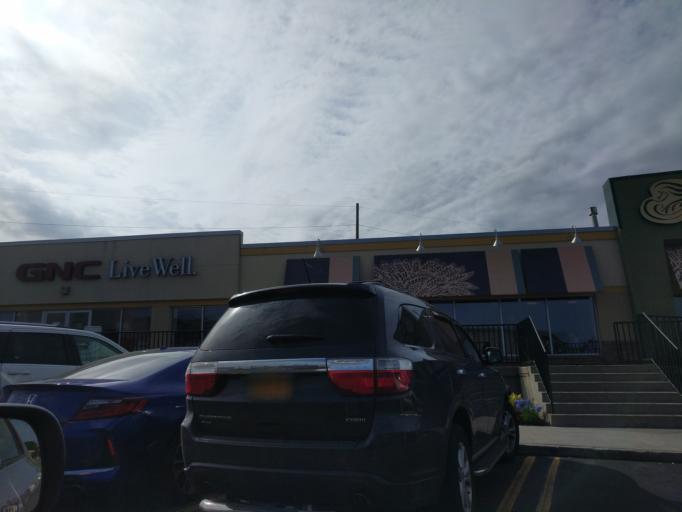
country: US
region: New York
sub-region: Nassau County
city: Inwood
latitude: 40.6271
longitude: -73.7394
